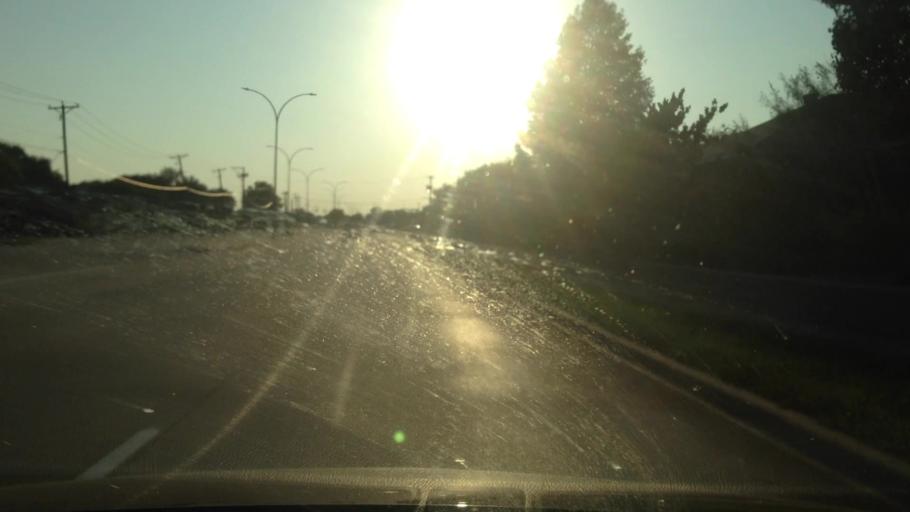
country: US
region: Texas
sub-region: Tarrant County
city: Dalworthington Gardens
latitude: 32.6450
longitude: -97.1105
